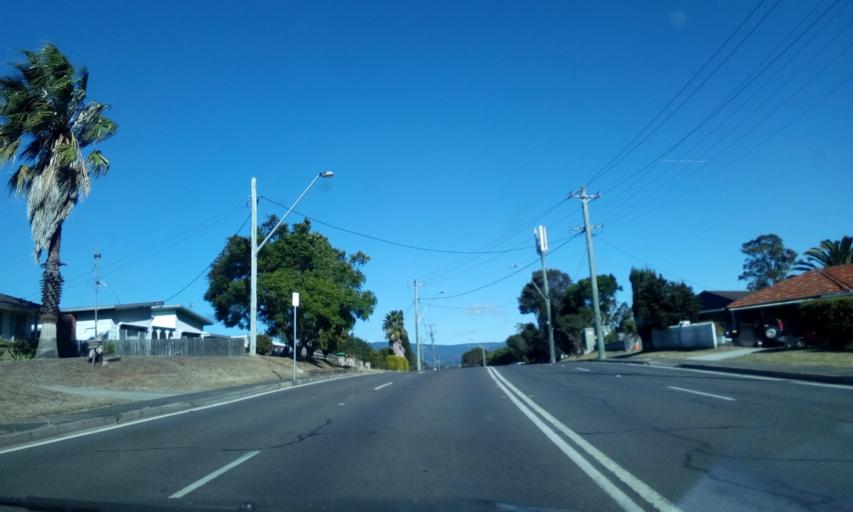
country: AU
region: New South Wales
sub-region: Wollongong
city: Dapto
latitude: -34.5104
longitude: 150.7863
